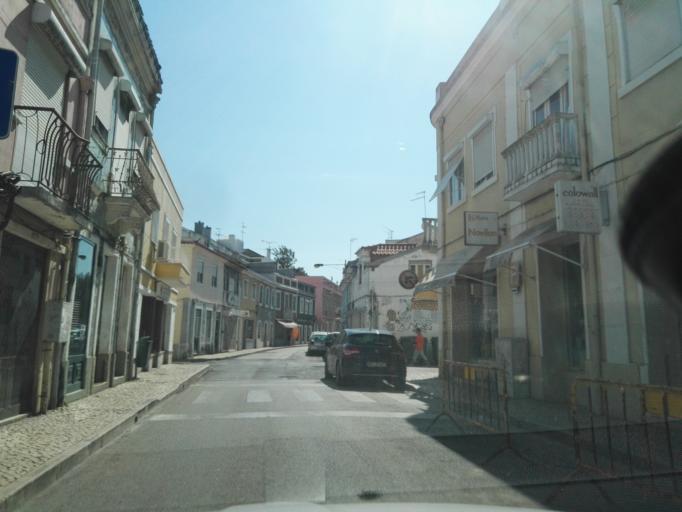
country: PT
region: Lisbon
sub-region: Vila Franca de Xira
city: Alhandra
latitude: 38.9262
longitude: -9.0092
